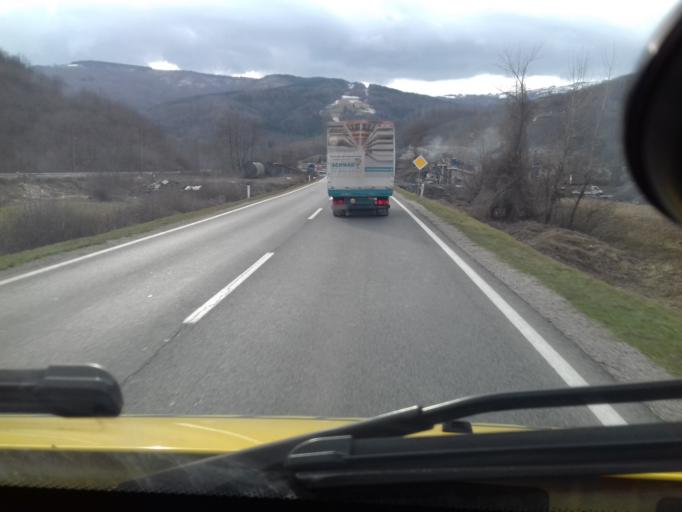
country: BA
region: Federation of Bosnia and Herzegovina
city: Zeljezno Polje
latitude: 44.3969
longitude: 17.9907
